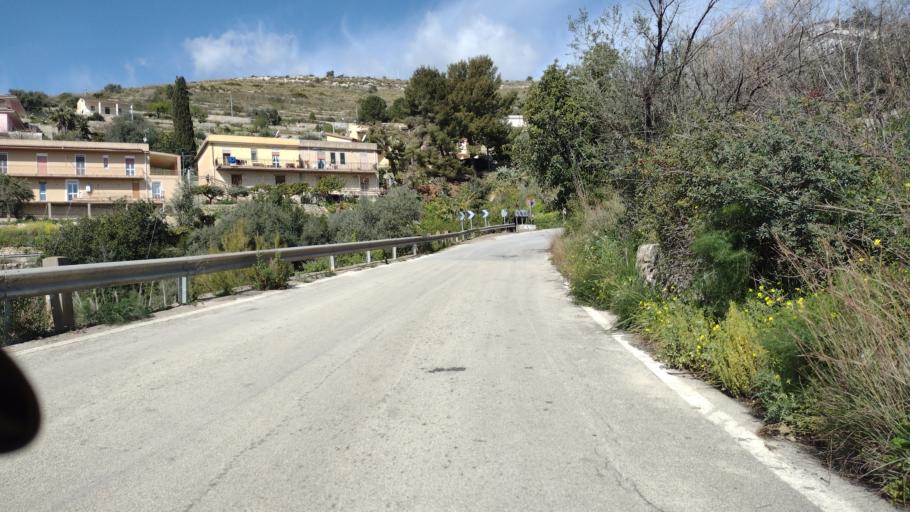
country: IT
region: Sicily
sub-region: Provincia di Siracusa
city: Noto
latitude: 36.9076
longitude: 15.0271
